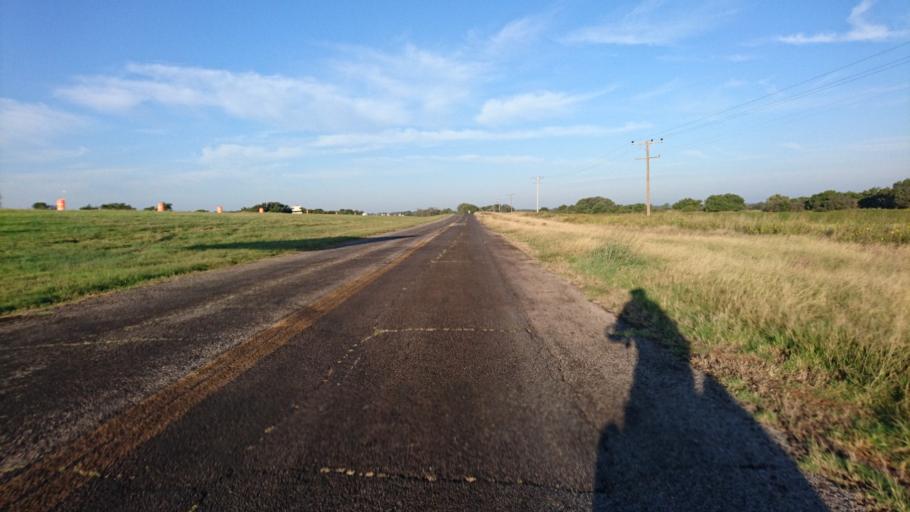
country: US
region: Oklahoma
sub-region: Beckham County
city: Sayre
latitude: 35.2625
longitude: -99.7010
